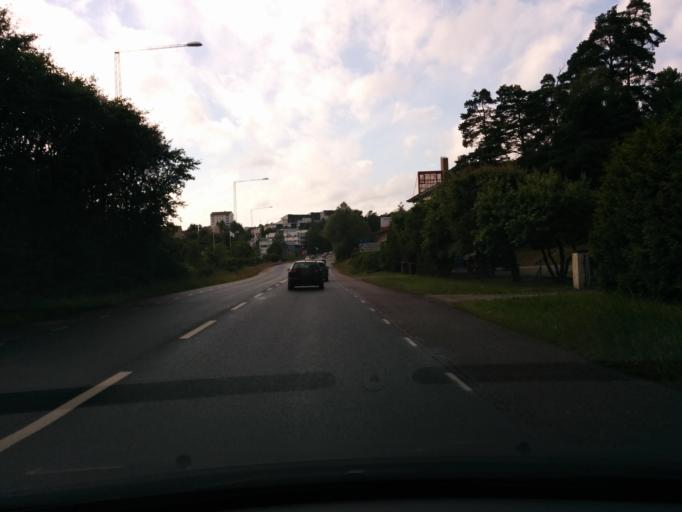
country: SE
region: Stockholm
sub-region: Sollentuna Kommun
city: Sollentuna
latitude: 59.4250
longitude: 18.0002
